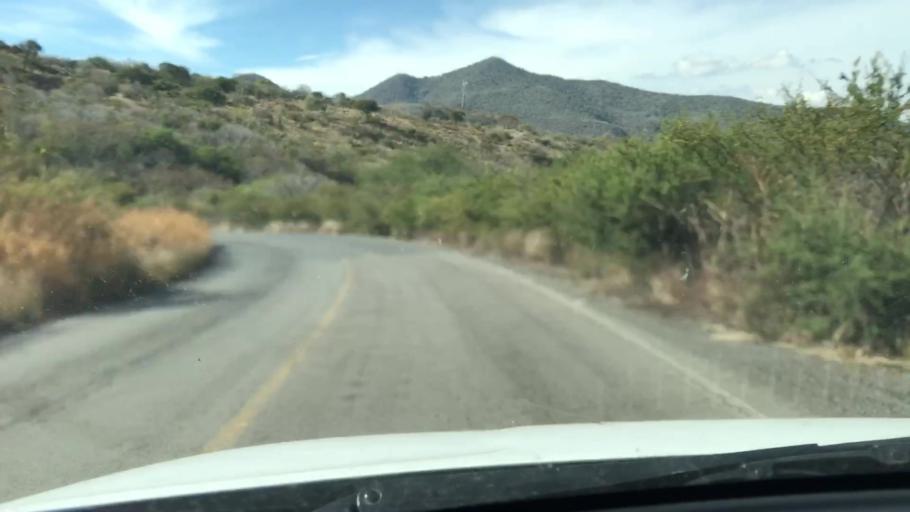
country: MX
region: Jalisco
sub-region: Zacoalco de Torres
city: Barranca de Otates (Barranca de Otatan)
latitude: 20.2518
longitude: -103.6719
